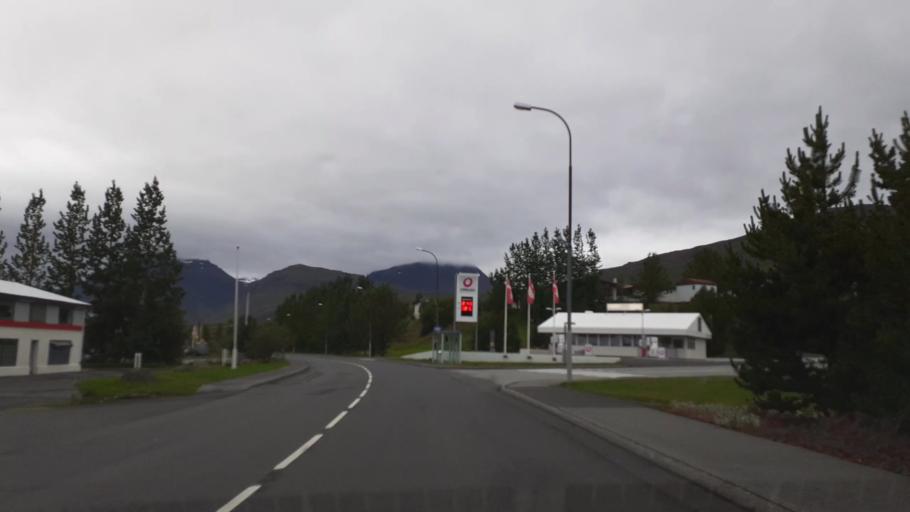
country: IS
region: East
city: Reydarfjoerdur
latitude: 65.0342
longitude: -14.2266
